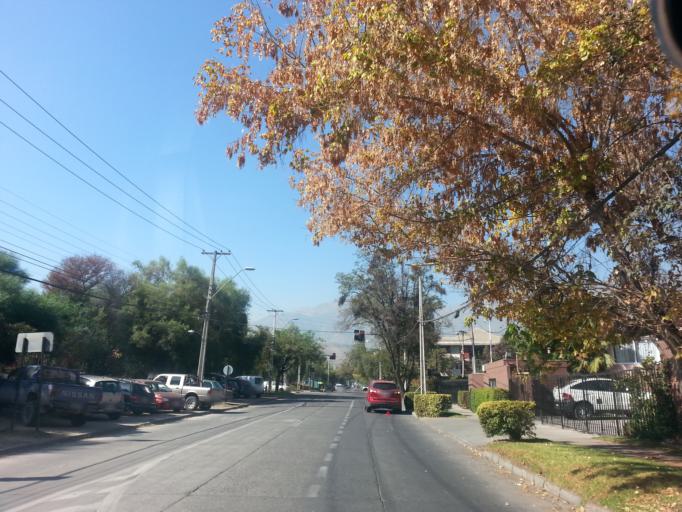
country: CL
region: Santiago Metropolitan
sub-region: Provincia de Santiago
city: Villa Presidente Frei, Nunoa, Santiago, Chile
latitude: -33.4351
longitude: -70.5511
